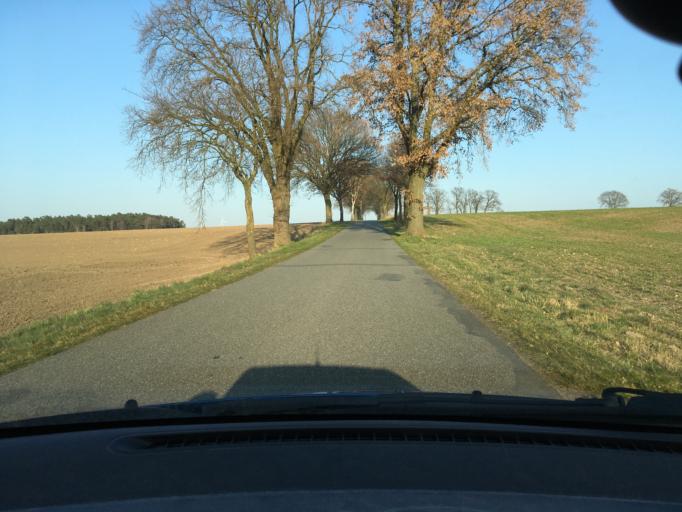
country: DE
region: Lower Saxony
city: Reinstorf
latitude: 53.2388
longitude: 10.6028
